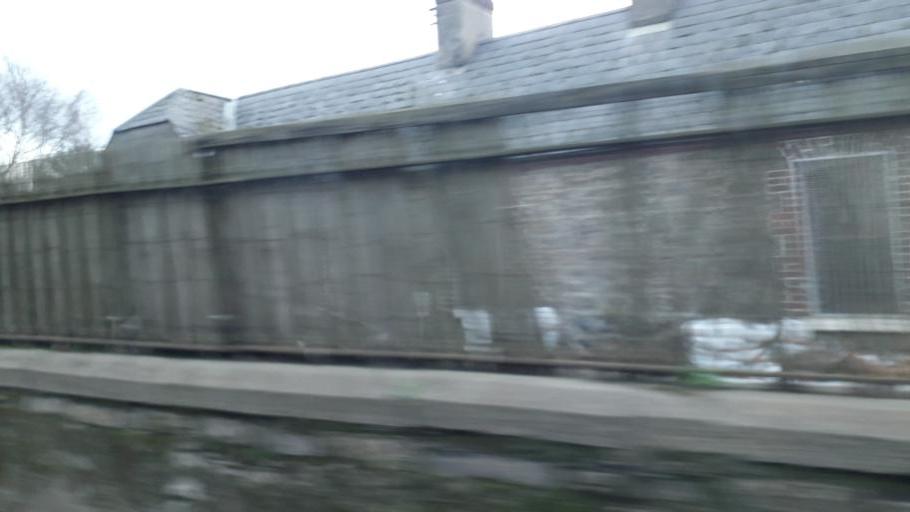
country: IE
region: Leinster
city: An Ros
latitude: 53.5292
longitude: -6.0914
